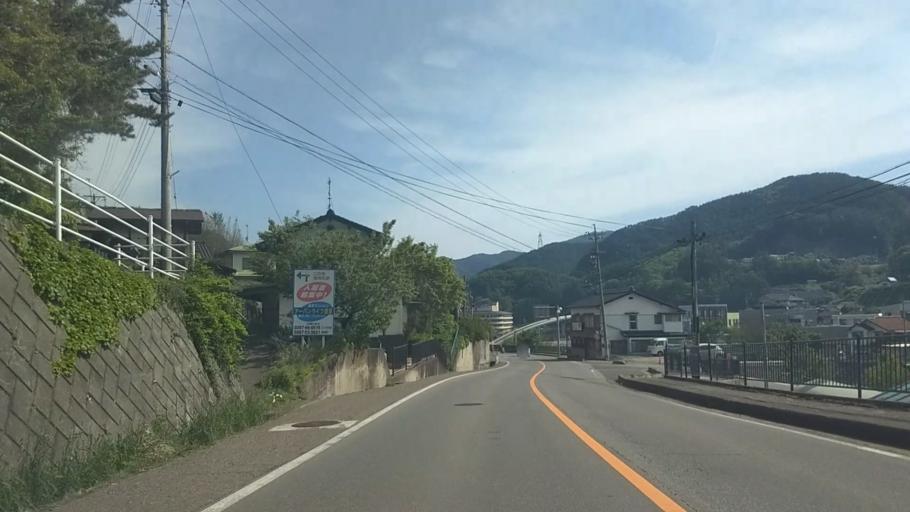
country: JP
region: Nagano
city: Saku
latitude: 36.0889
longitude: 138.4811
